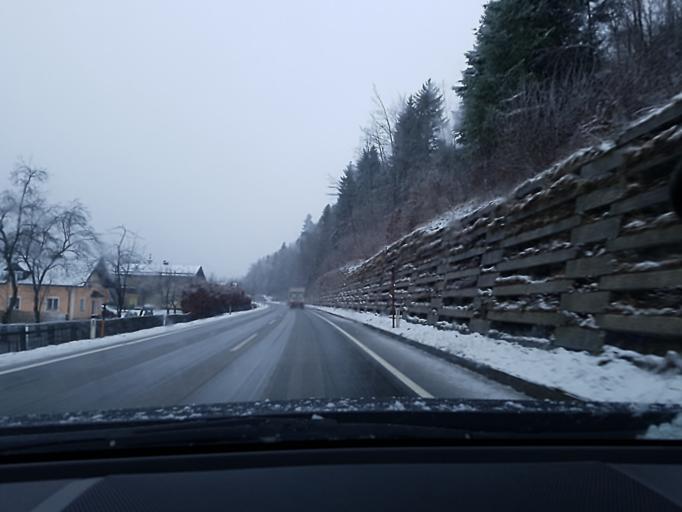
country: AT
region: Salzburg
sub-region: Politischer Bezirk Hallein
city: Scheffau am Tennengebirge
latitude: 47.5794
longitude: 13.2633
